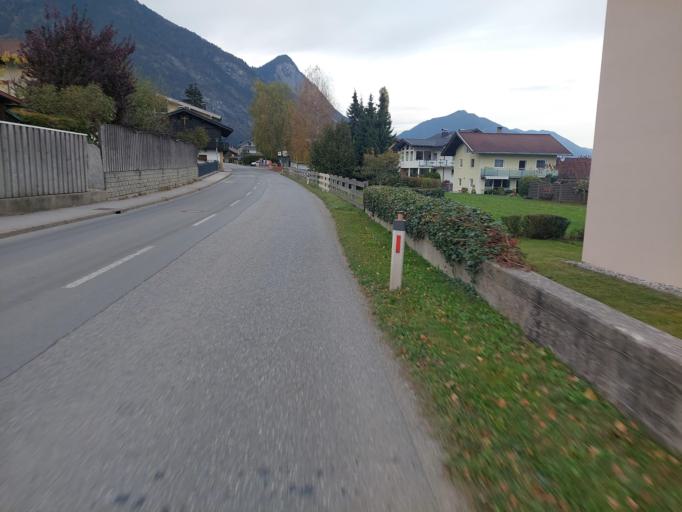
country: AT
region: Tyrol
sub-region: Politischer Bezirk Kufstein
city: Munster
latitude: 47.4131
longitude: 11.8308
